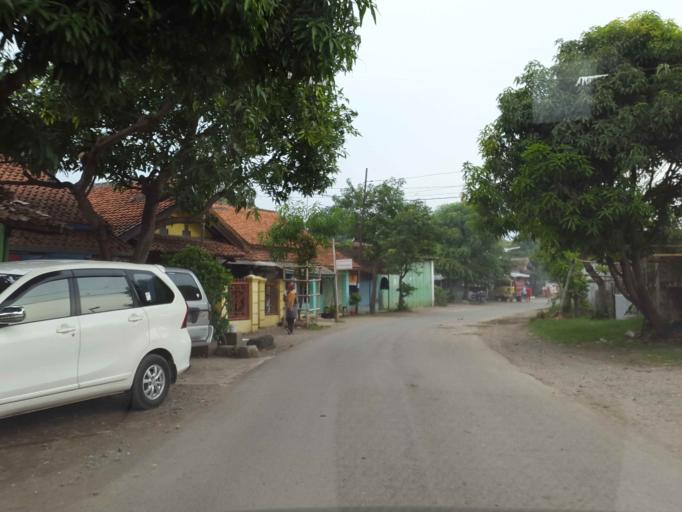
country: ID
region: Central Java
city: Dukuhturi
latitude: -6.9725
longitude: 109.0627
